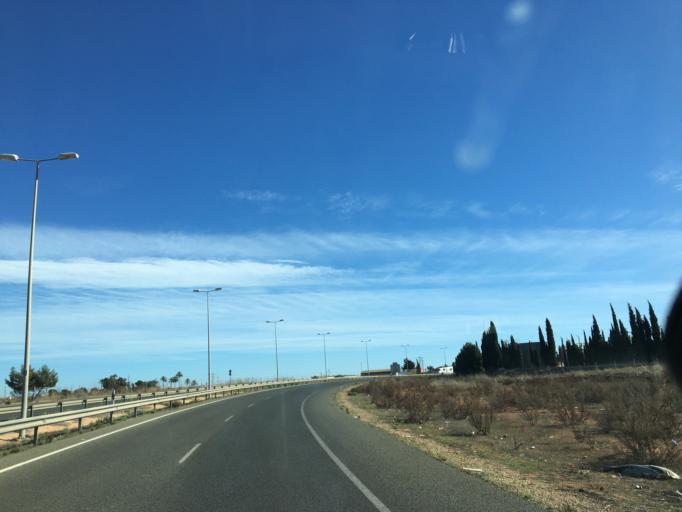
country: ES
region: Murcia
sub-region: Murcia
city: Cartagena
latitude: 37.6394
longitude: -0.9931
